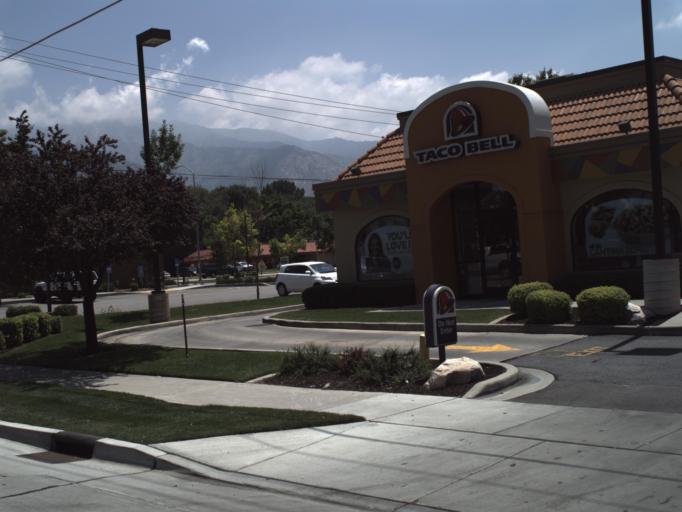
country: US
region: Utah
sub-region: Weber County
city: Ogden
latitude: 41.2443
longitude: -111.9741
